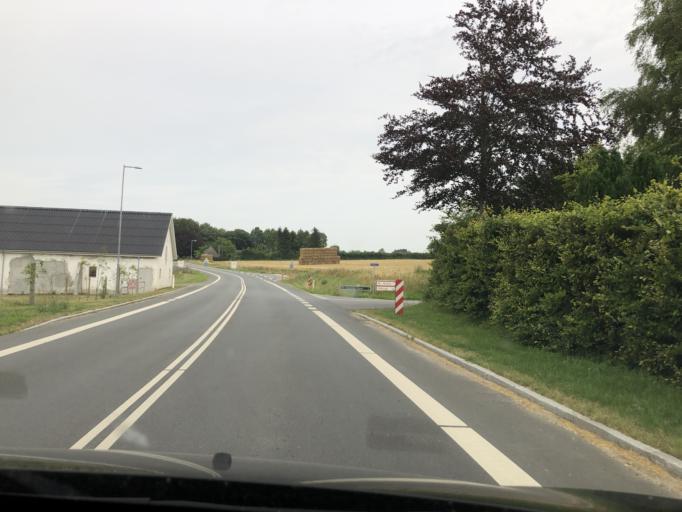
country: DK
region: South Denmark
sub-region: Assens Kommune
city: Glamsbjerg
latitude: 55.2525
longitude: 10.1345
